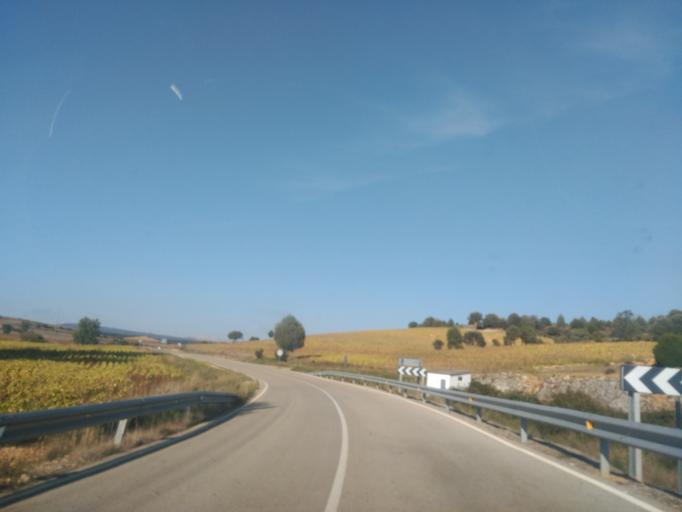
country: ES
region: Castille and Leon
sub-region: Provincia de Soria
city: Alcubilla de Avellaneda
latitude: 41.7446
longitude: -3.2851
